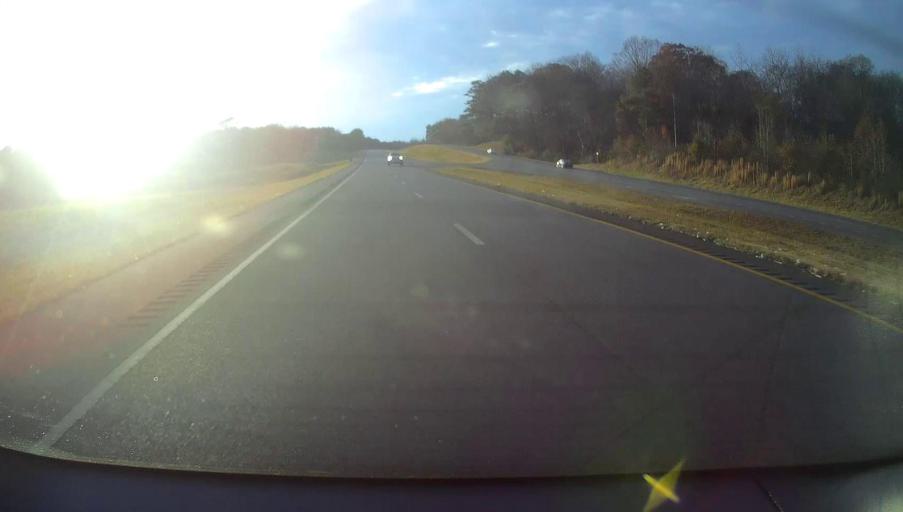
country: US
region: Alabama
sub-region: Blount County
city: Blountsville
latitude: 34.1608
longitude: -86.4874
